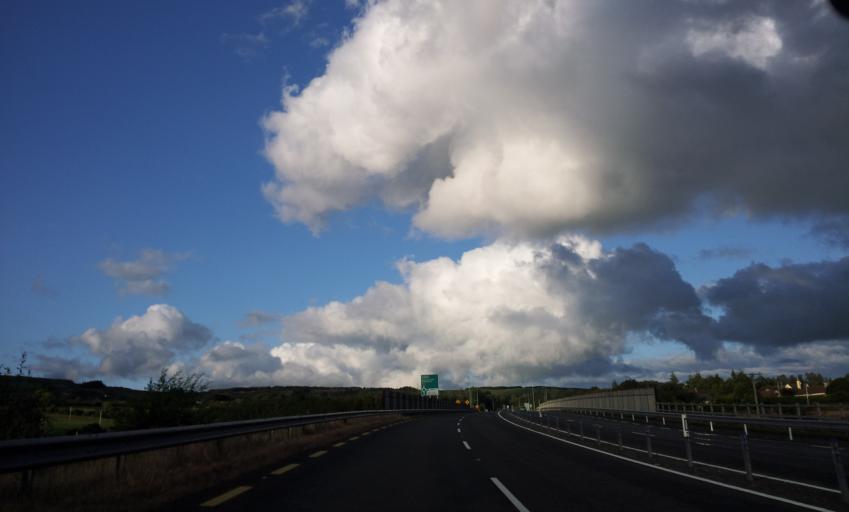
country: IE
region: Munster
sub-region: Ciarrai
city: Castleisland
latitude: 52.2589
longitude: -9.4683
